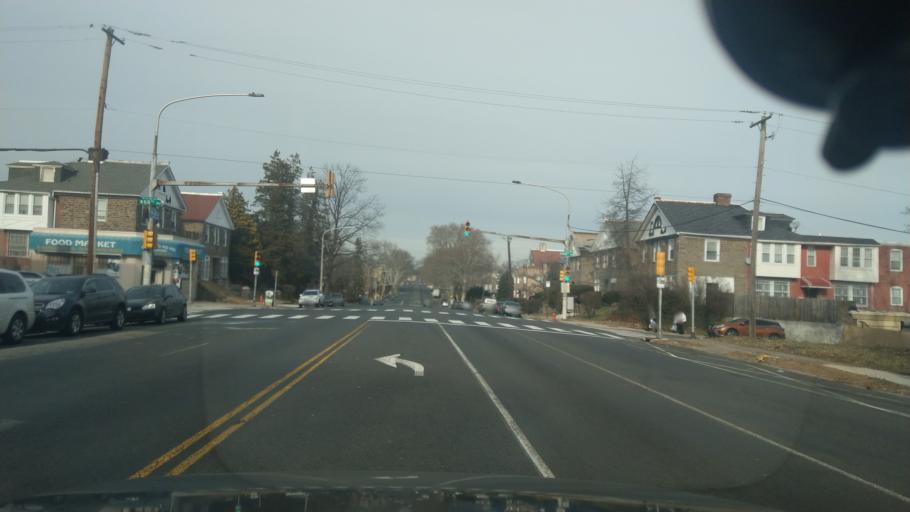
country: US
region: Pennsylvania
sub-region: Montgomery County
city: Wyncote
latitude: 40.0563
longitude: -75.1409
